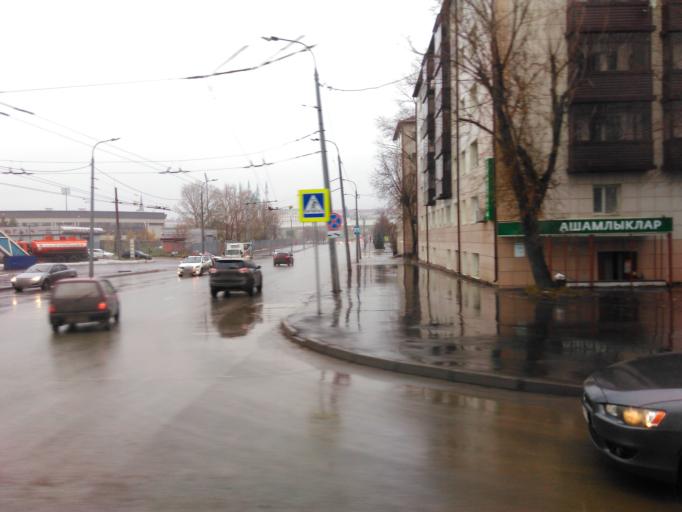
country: RU
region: Tatarstan
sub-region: Gorod Kazan'
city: Kazan
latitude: 55.7937
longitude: 49.0964
